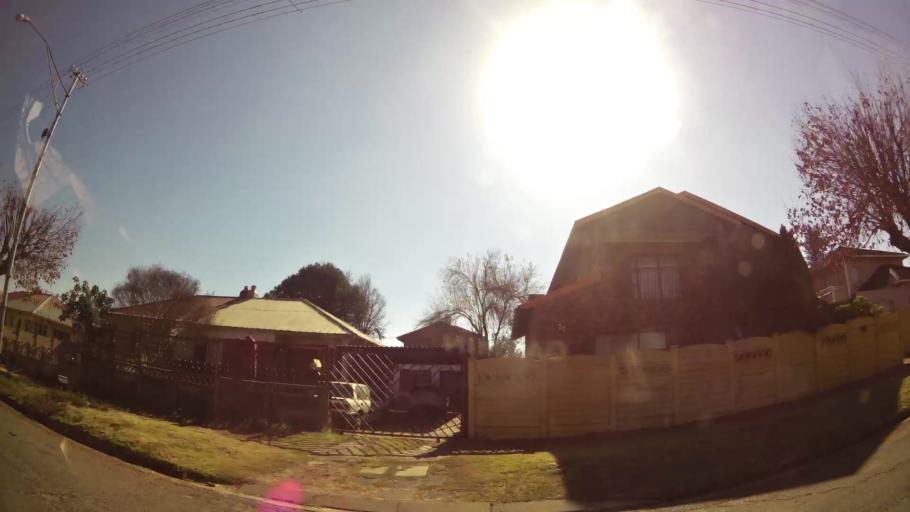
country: ZA
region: Gauteng
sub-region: City of Johannesburg Metropolitan Municipality
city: Johannesburg
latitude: -26.1890
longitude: 27.9756
